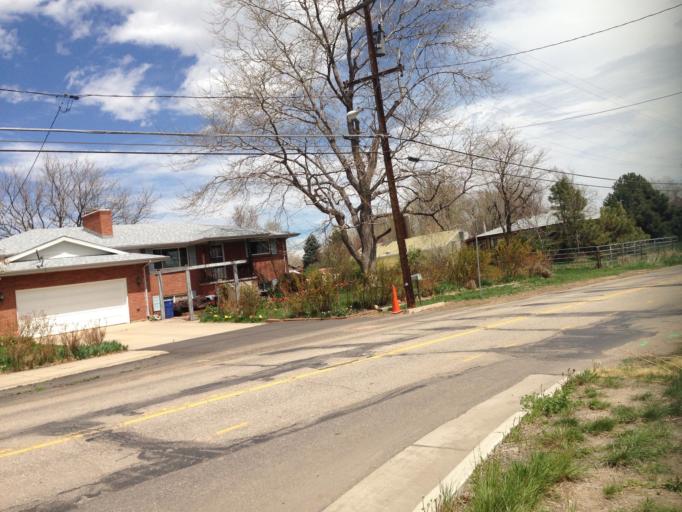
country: US
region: Colorado
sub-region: Jefferson County
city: Applewood
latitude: 39.7908
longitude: -105.1324
